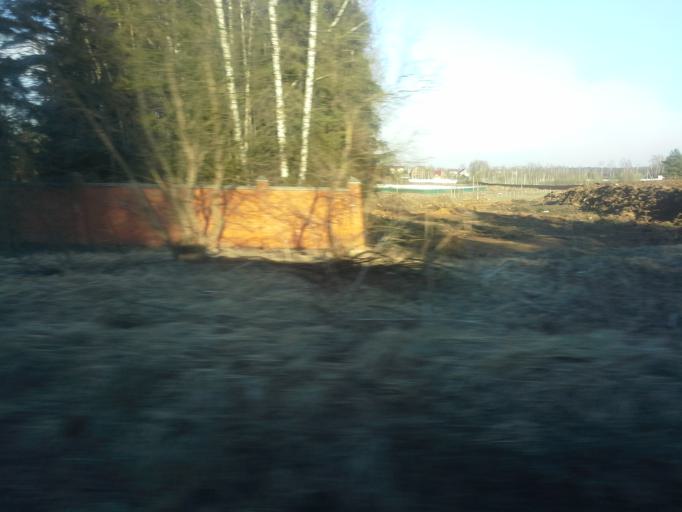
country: RU
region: Moskovskaya
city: Yermolino
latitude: 56.1271
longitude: 37.5192
